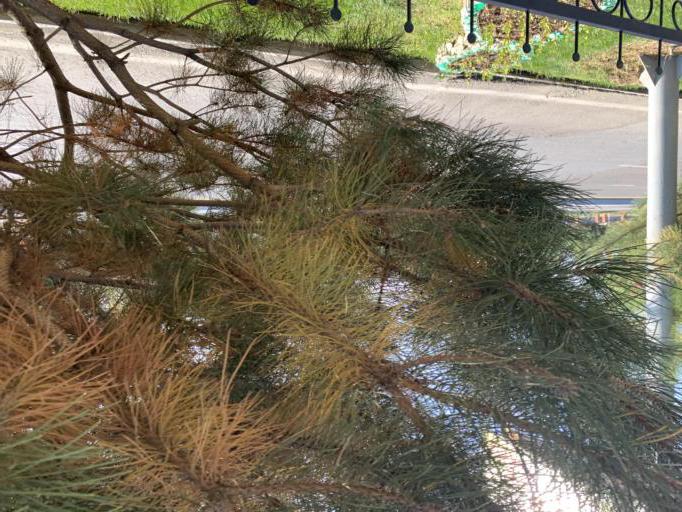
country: UZ
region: Namangan
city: Namangan Shahri
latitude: 40.9959
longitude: 71.5918
